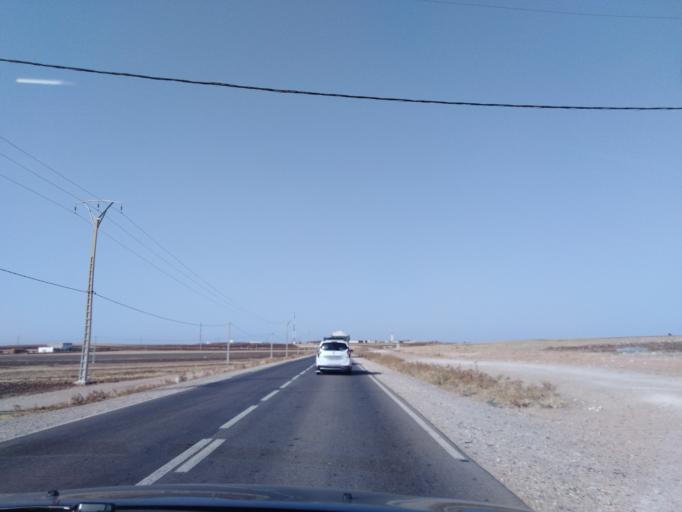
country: MA
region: Doukkala-Abda
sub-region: Safi
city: Safi
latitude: 32.2811
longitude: -8.9194
